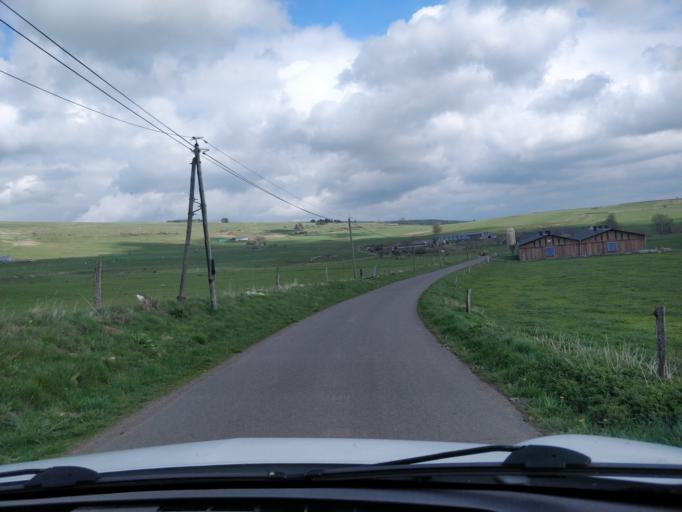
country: FR
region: Auvergne
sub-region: Departement du Cantal
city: Allanche
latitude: 45.2098
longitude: 2.9491
